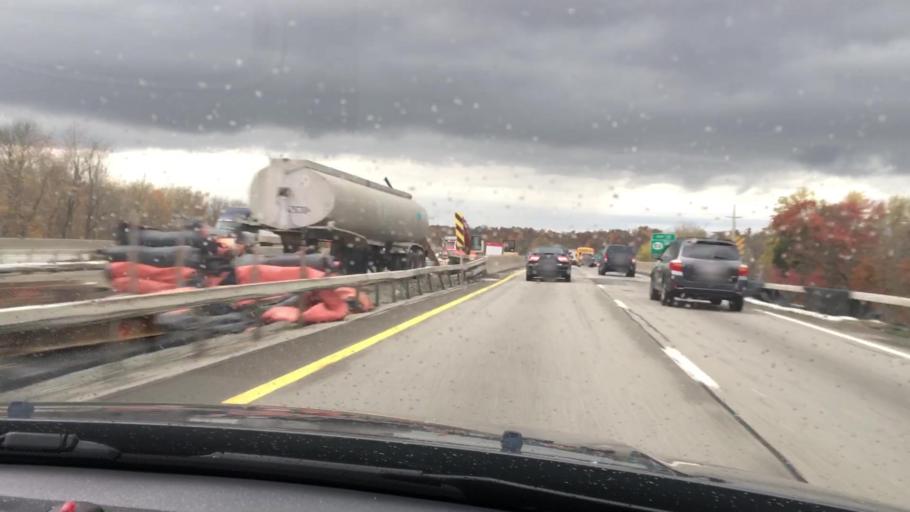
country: US
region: New York
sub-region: Dutchess County
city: Fishkill
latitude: 41.5249
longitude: -73.9118
